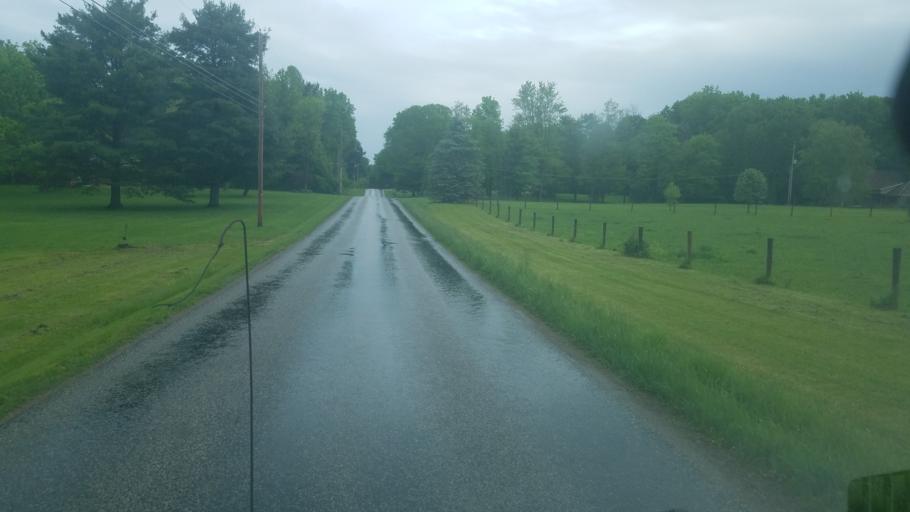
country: US
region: Ohio
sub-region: Wayne County
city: Smithville
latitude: 40.8189
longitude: -81.8774
